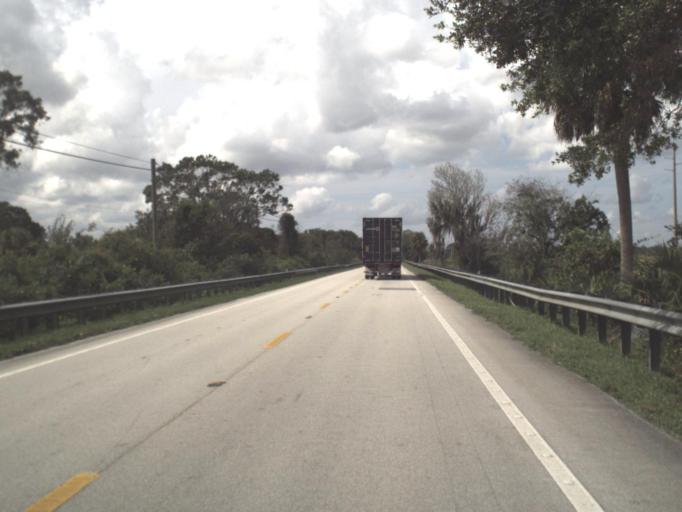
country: US
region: Florida
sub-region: Highlands County
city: Lake Placid
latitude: 27.2084
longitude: -81.2680
